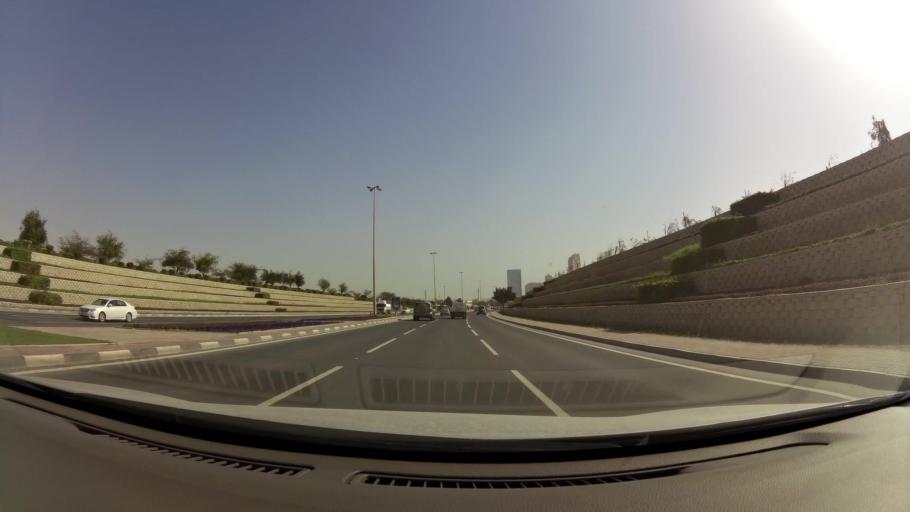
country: QA
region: Baladiyat ad Dawhah
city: Doha
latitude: 25.3158
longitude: 51.5071
